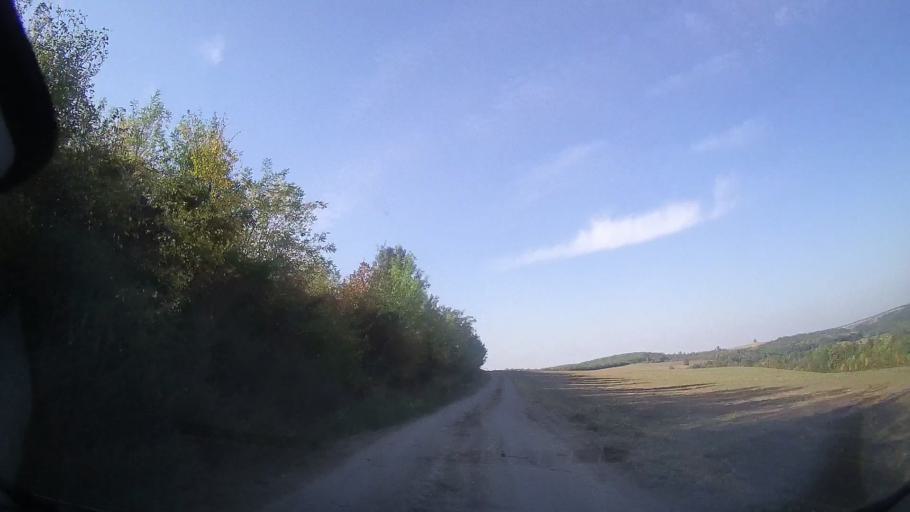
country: RO
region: Timis
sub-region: Comuna Bogda
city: Bogda
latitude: 45.9126
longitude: 21.6049
